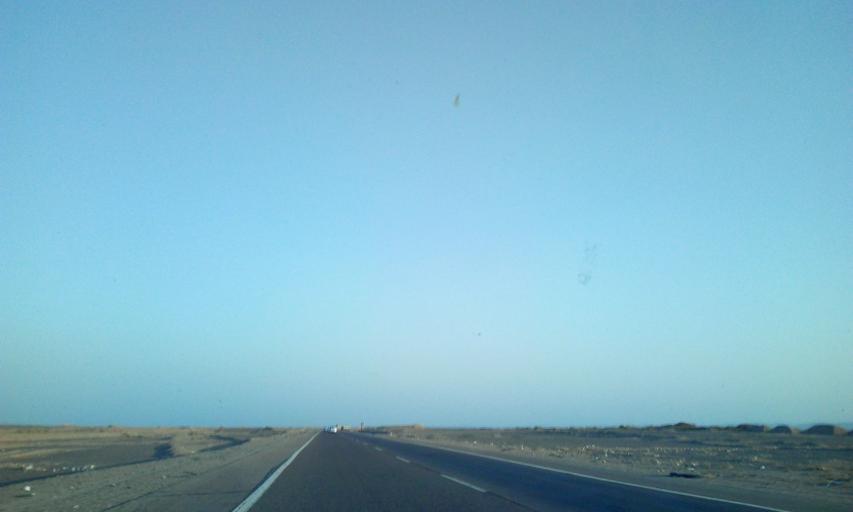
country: EG
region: South Sinai
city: Tor
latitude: 27.9101
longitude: 33.3959
